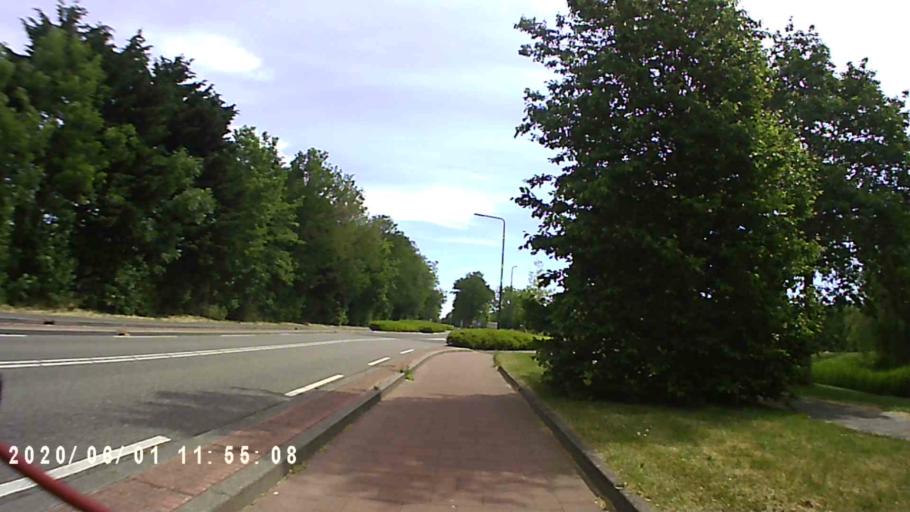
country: NL
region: Friesland
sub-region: Gemeente Harlingen
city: Harlingen
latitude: 53.1633
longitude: 5.4316
